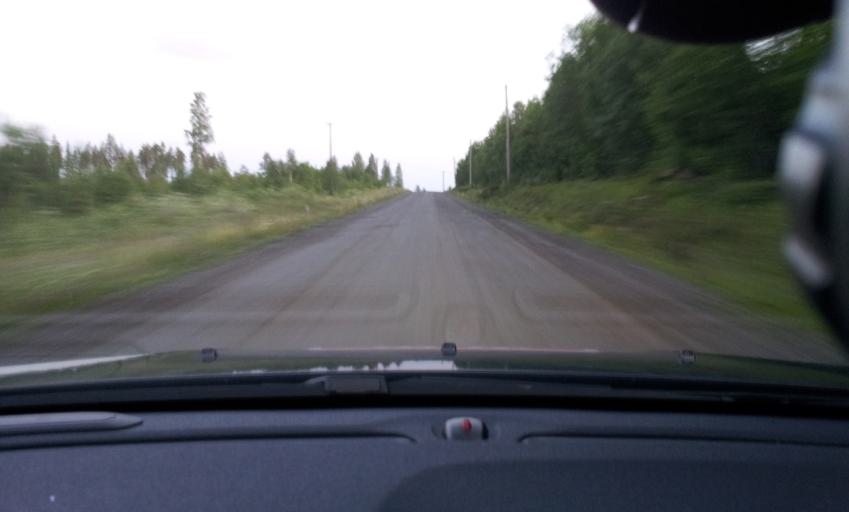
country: SE
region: Jaemtland
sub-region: Ragunda Kommun
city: Hammarstrand
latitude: 62.9021
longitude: 16.0927
